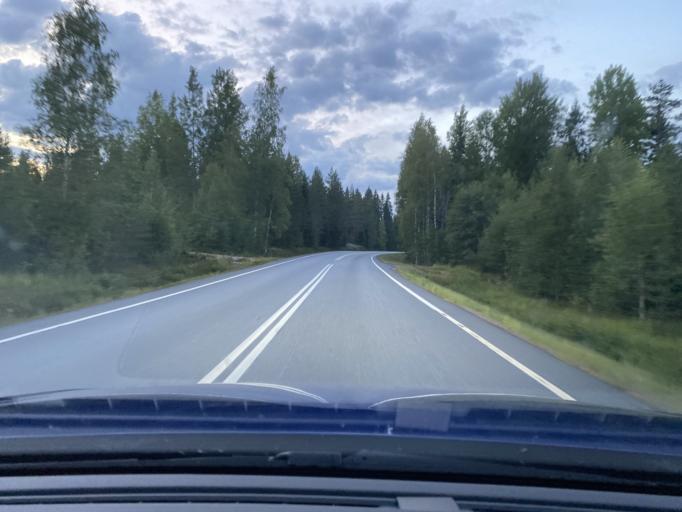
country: FI
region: Southern Ostrobothnia
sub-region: Suupohja
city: Kauhajoki
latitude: 62.2429
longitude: 22.2721
